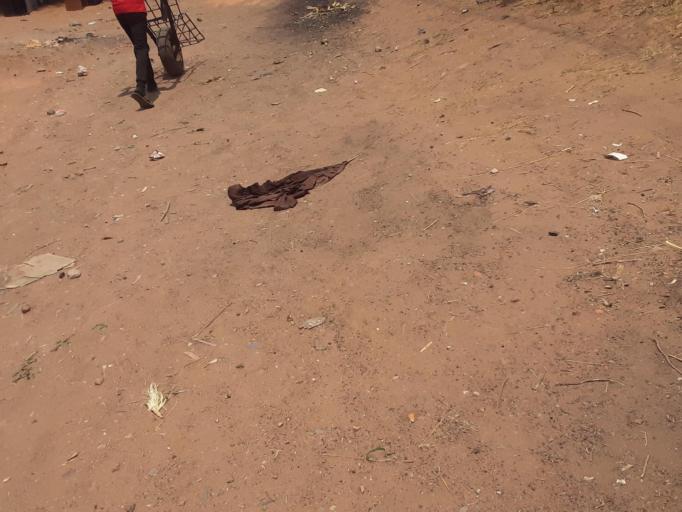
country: ZM
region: Lusaka
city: Lusaka
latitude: -15.3613
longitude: 28.3020
